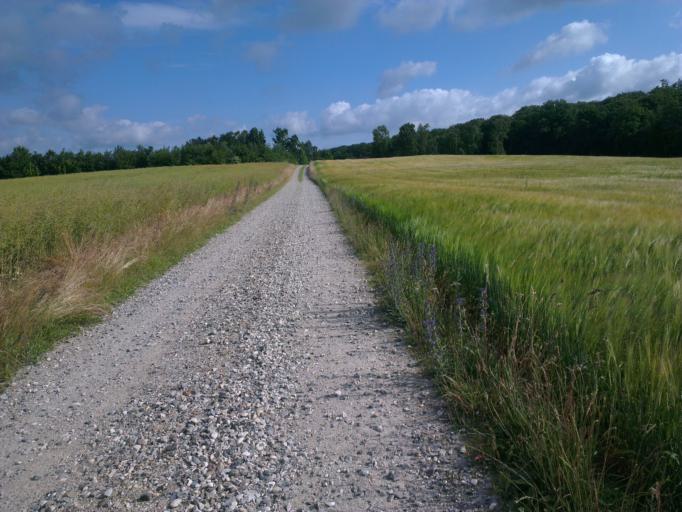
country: DK
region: Capital Region
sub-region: Frederikssund Kommune
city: Jaegerspris
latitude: 55.8807
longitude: 11.9798
